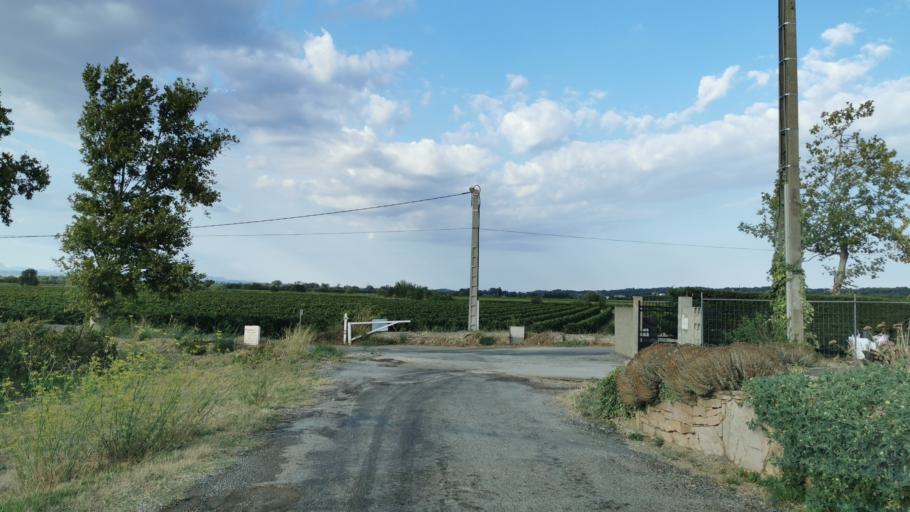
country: FR
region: Languedoc-Roussillon
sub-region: Departement de l'Aude
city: Nevian
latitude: 43.2171
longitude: 2.8990
